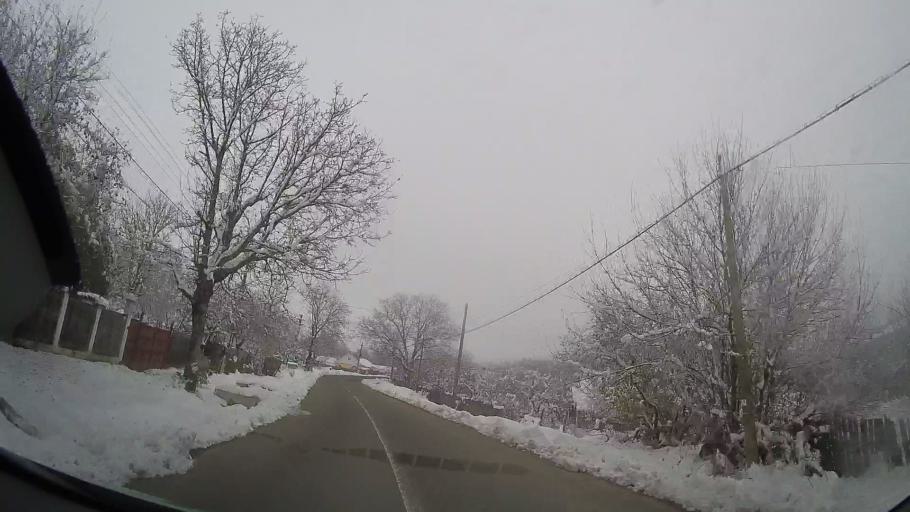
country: RO
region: Neamt
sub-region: Comuna Bozieni
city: Bozieni
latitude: 46.8382
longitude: 27.1514
